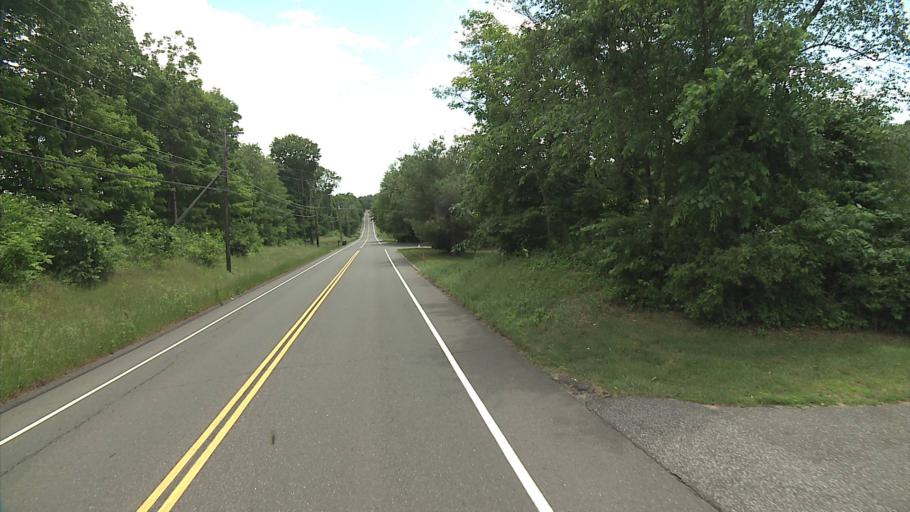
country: US
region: Connecticut
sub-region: Litchfield County
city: Watertown
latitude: 41.6184
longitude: -73.1298
